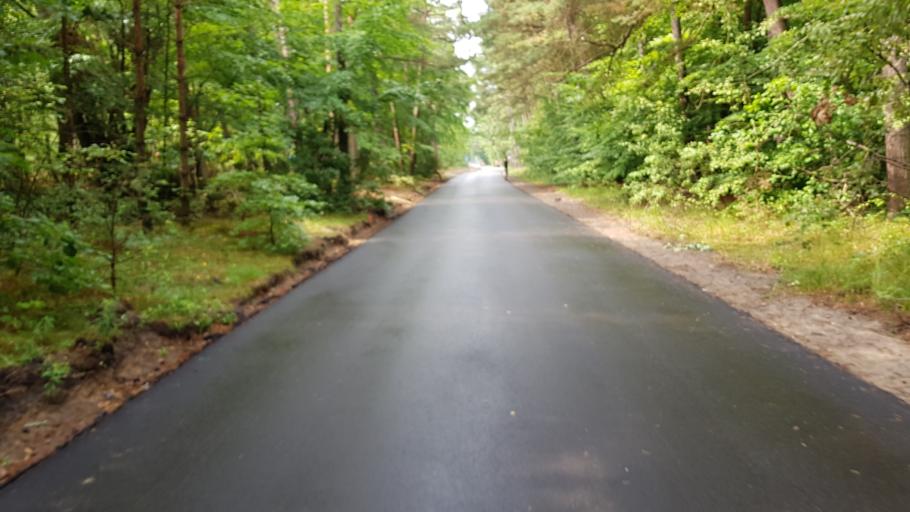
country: PL
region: West Pomeranian Voivodeship
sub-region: Powiat slawienski
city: Darlowo
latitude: 54.5122
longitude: 16.4753
